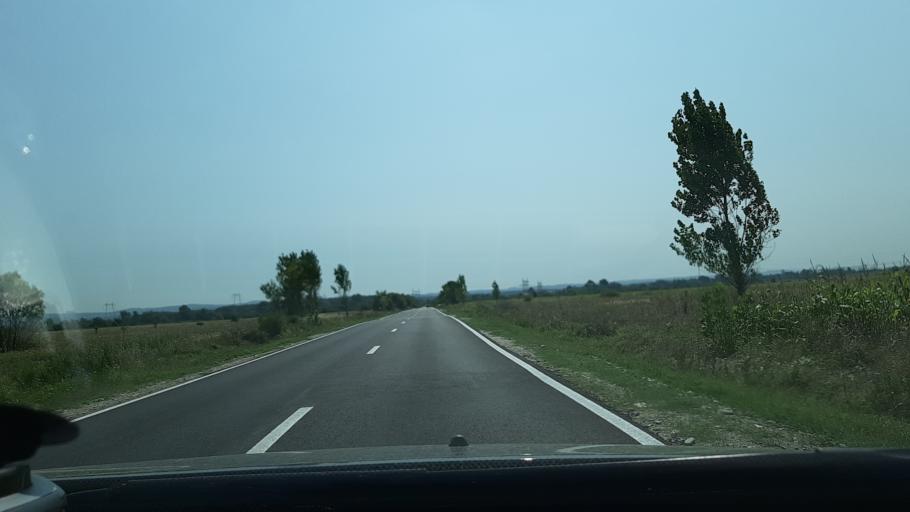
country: RO
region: Gorj
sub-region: Comuna Targu Carbunesti
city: Pojogeni
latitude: 45.0062
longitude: 23.4833
